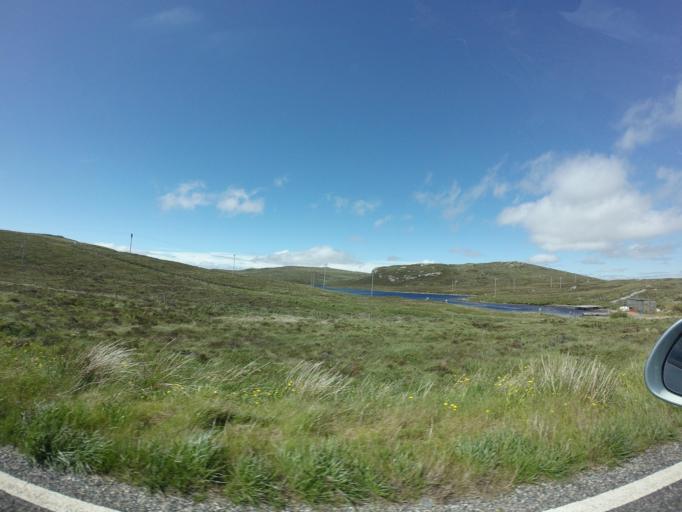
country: GB
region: Scotland
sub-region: Eilean Siar
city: Stornoway
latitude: 58.1238
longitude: -6.5087
